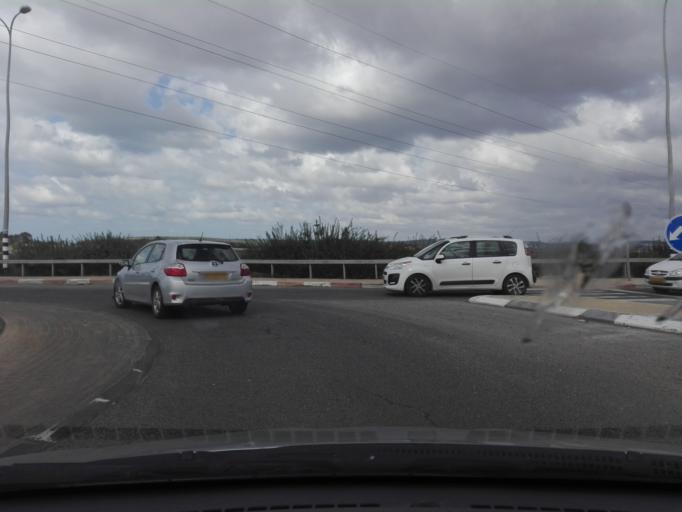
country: IL
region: Haifa
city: Qesarya
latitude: 32.5108
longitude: 34.9574
